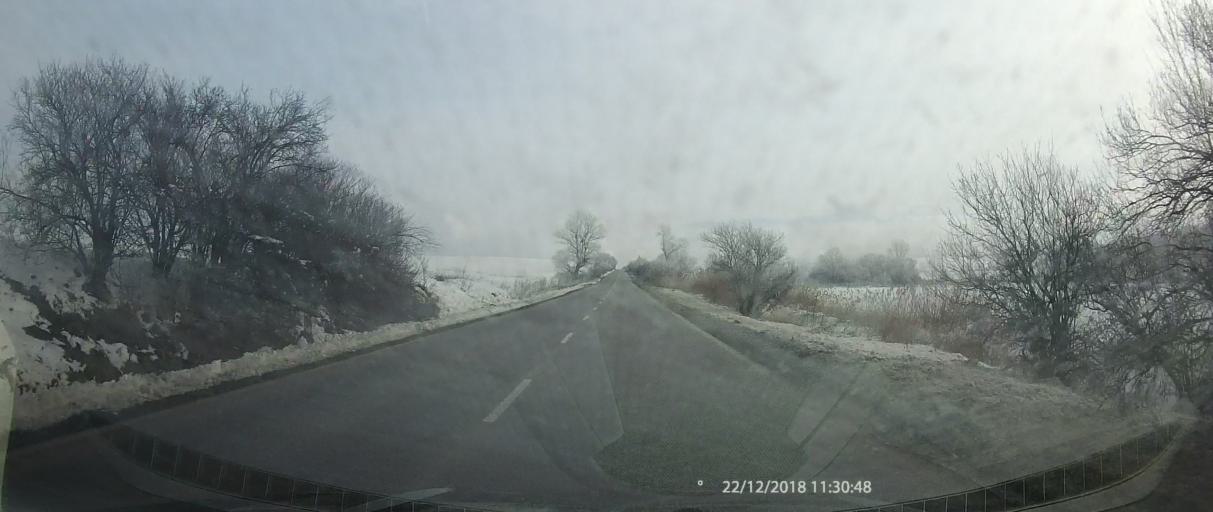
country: BG
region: Kyustendil
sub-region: Obshtina Bobovdol
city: Bobovdol
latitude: 42.2737
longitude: 22.9807
